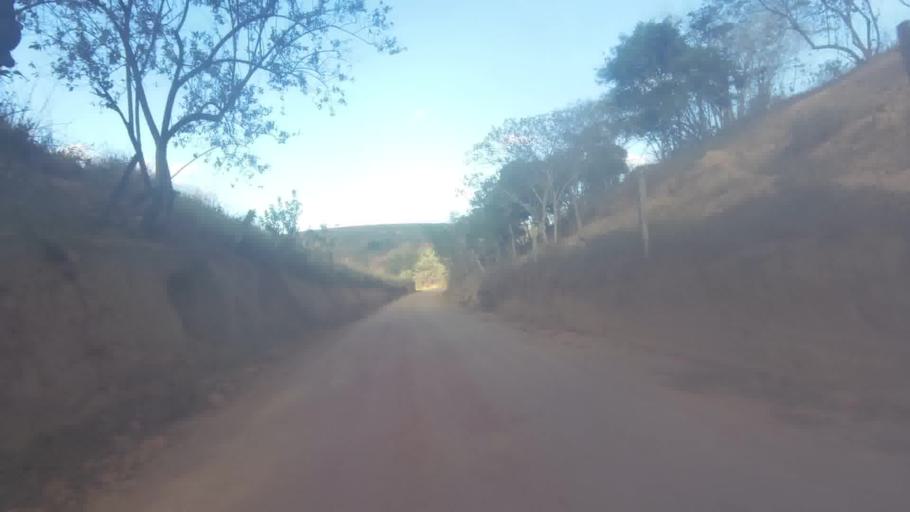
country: BR
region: Espirito Santo
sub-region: Mimoso Do Sul
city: Mimoso do Sul
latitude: -21.0861
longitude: -41.1438
